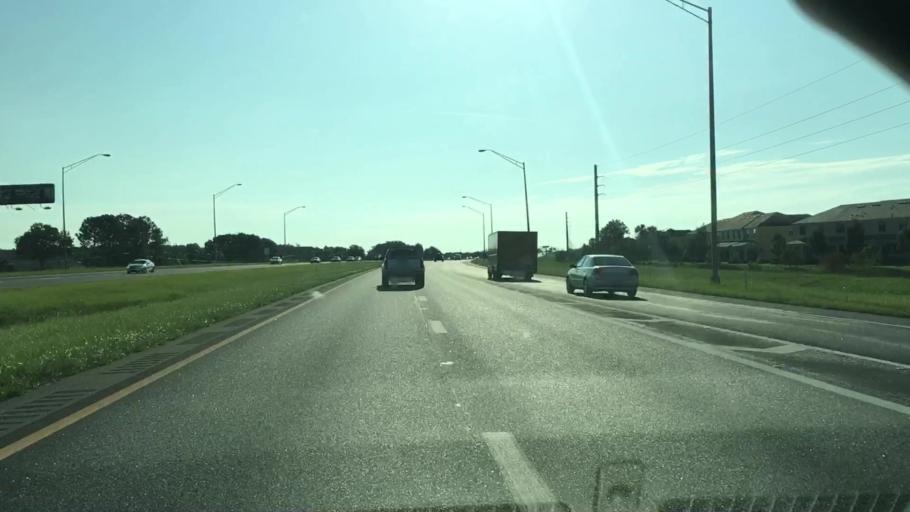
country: US
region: Florida
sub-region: Orange County
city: Meadow Woods
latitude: 28.3692
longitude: -81.3616
